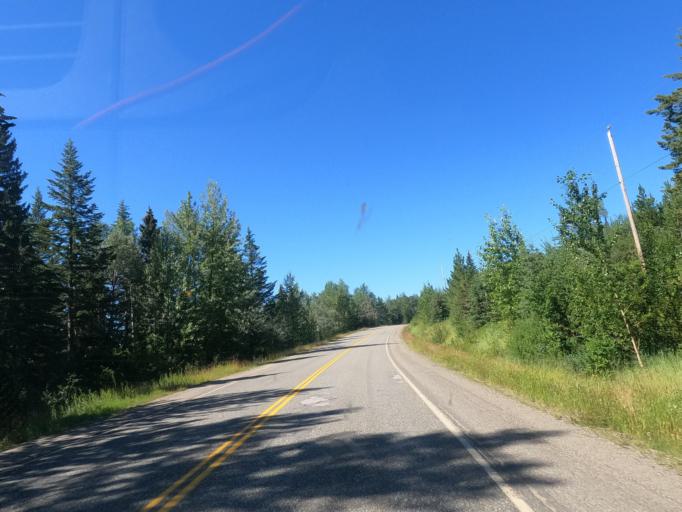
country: CA
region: British Columbia
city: Quesnel
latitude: 53.0288
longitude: -122.0132
